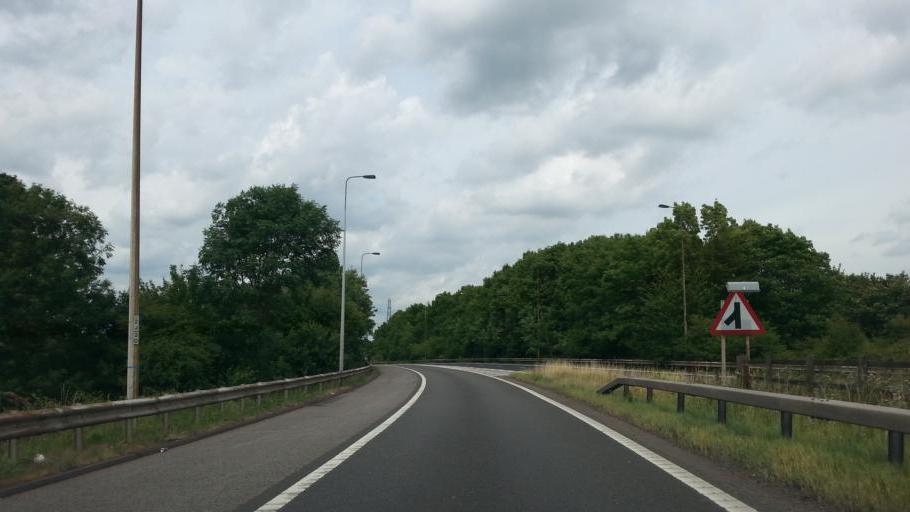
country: GB
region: England
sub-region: Warwickshire
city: Bedworth
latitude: 52.4401
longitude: -1.4278
